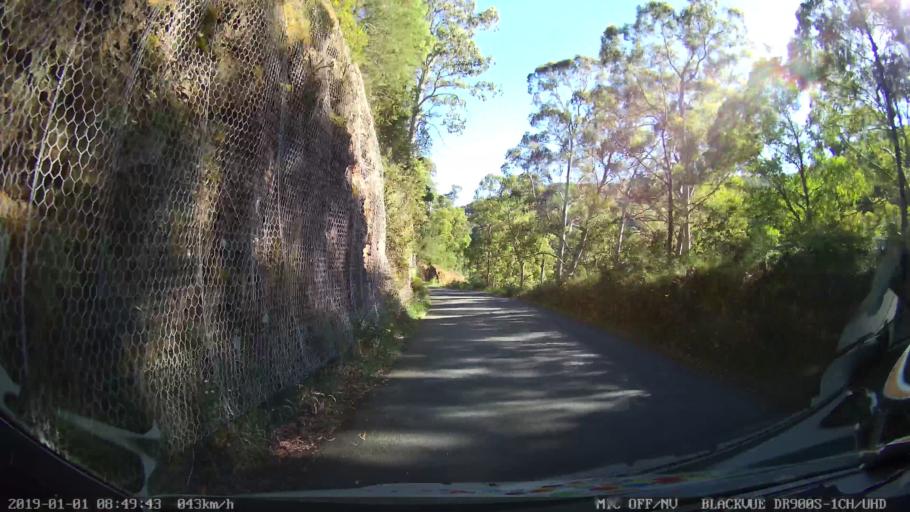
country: AU
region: New South Wales
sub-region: Snowy River
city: Jindabyne
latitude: -36.2807
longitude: 148.2010
